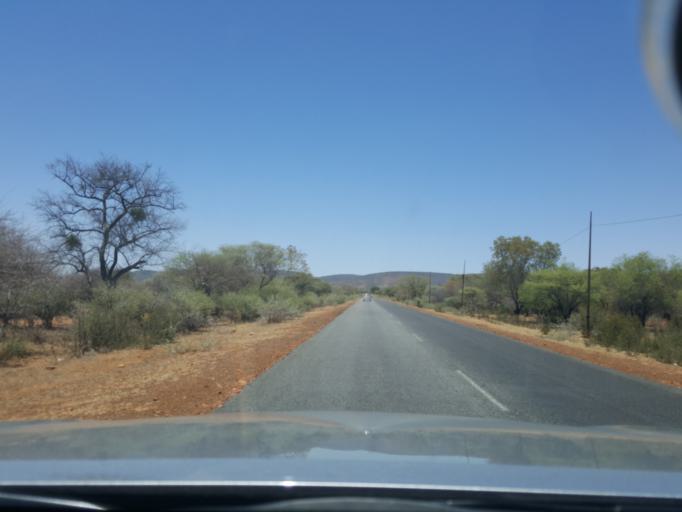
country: BW
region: South East
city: Lobatse
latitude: -25.2581
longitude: 25.9282
